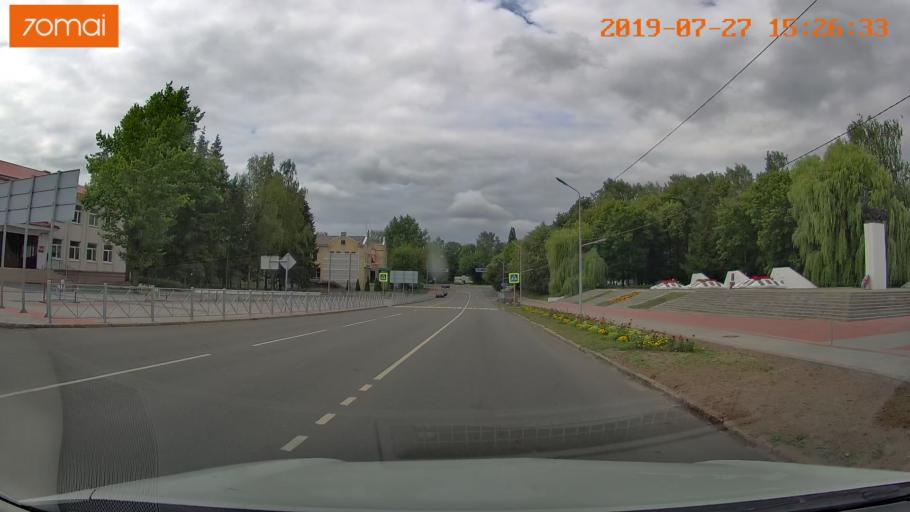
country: RU
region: Kaliningrad
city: Nesterov
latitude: 54.6314
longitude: 22.5716
